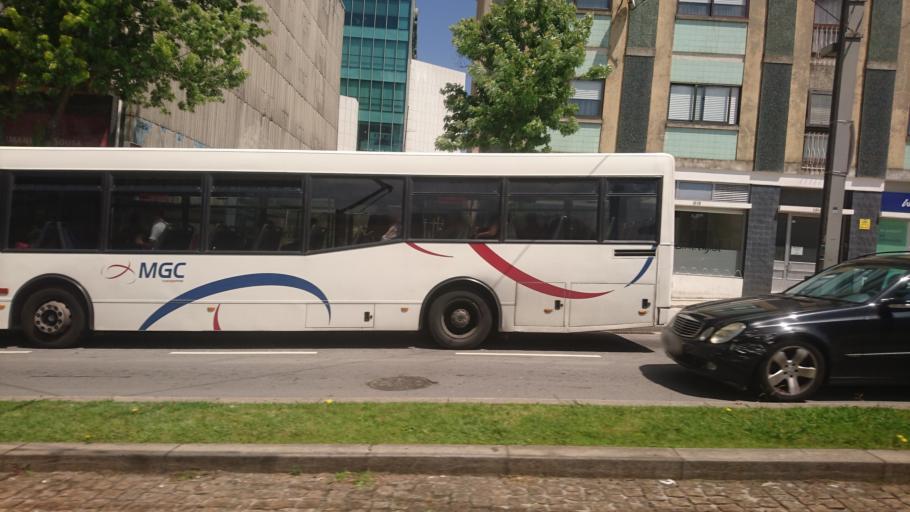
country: PT
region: Porto
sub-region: Vila Nova de Gaia
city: Vila Nova de Gaia
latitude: 41.1252
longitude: -8.6056
